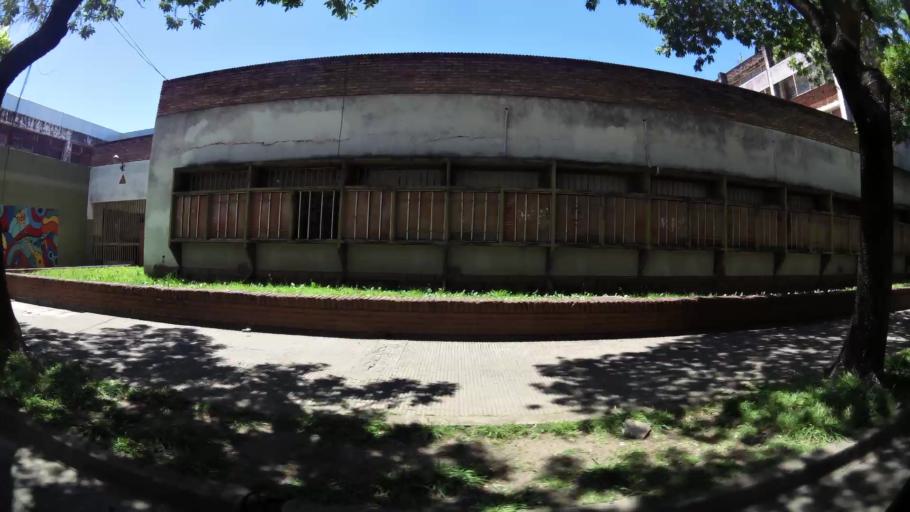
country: AR
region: Santa Fe
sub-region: Departamento de Rosario
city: Rosario
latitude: -32.9418
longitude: -60.7022
